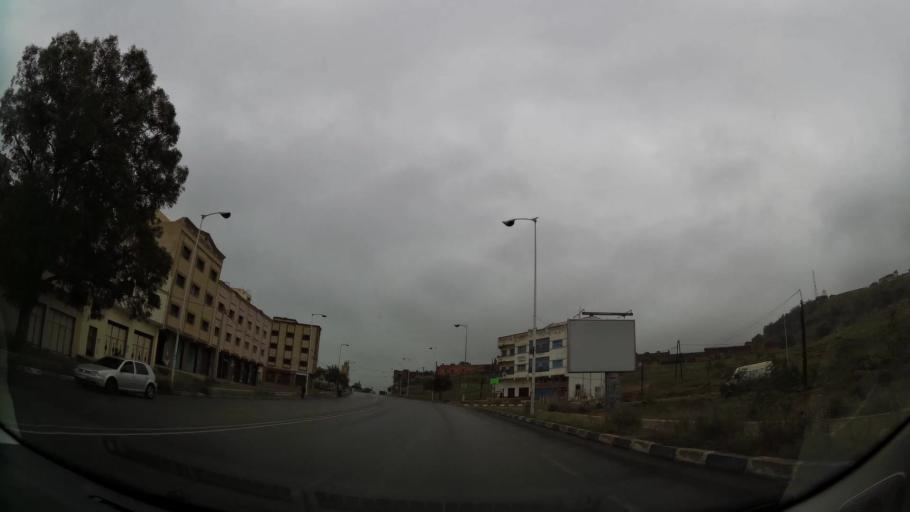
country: MA
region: Oriental
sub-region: Nador
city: Nador
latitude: 35.1898
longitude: -2.9308
